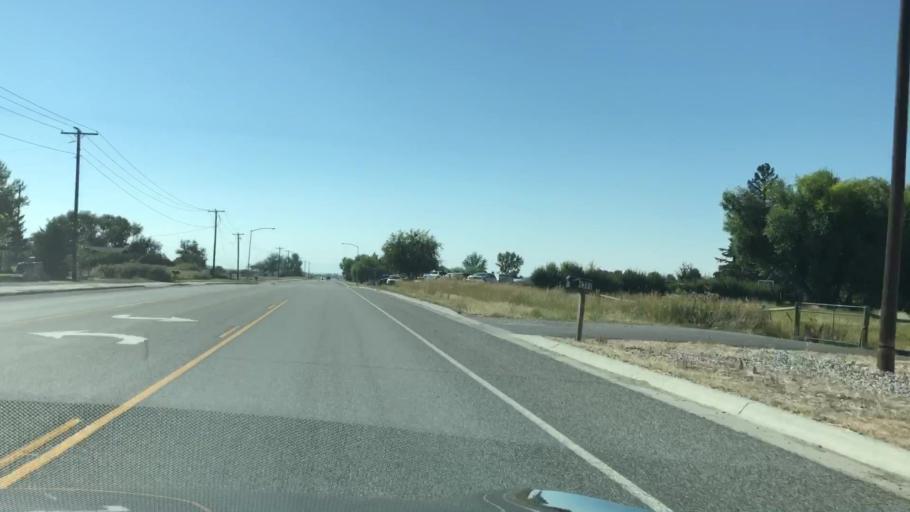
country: US
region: Montana
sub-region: Gallatin County
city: Bozeman
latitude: 45.7293
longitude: -111.0953
